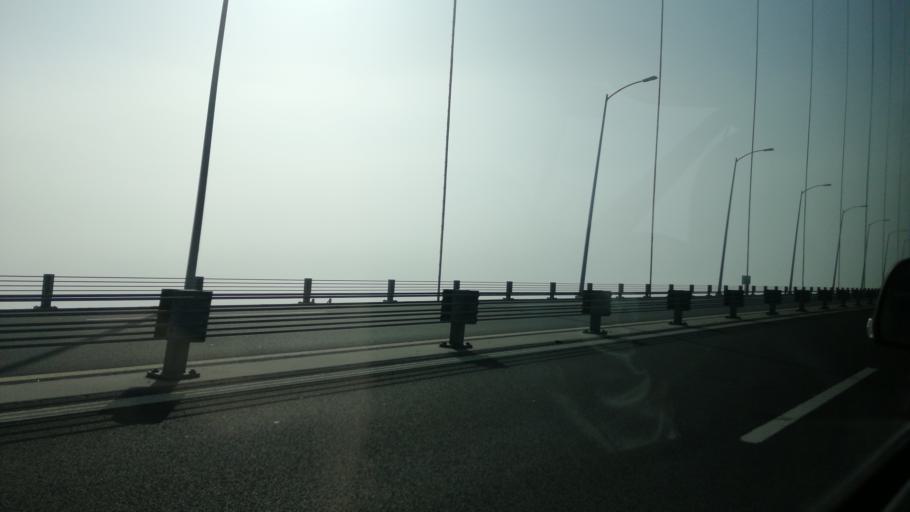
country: TR
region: Kocaeli
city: Tavsanli
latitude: 40.7655
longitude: 29.5174
